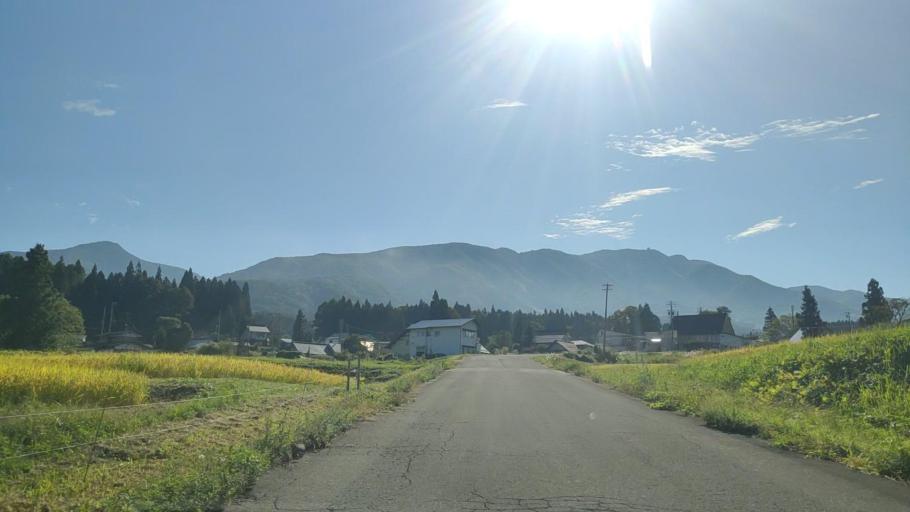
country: JP
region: Nagano
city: Iiyama
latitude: 36.8042
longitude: 138.4308
